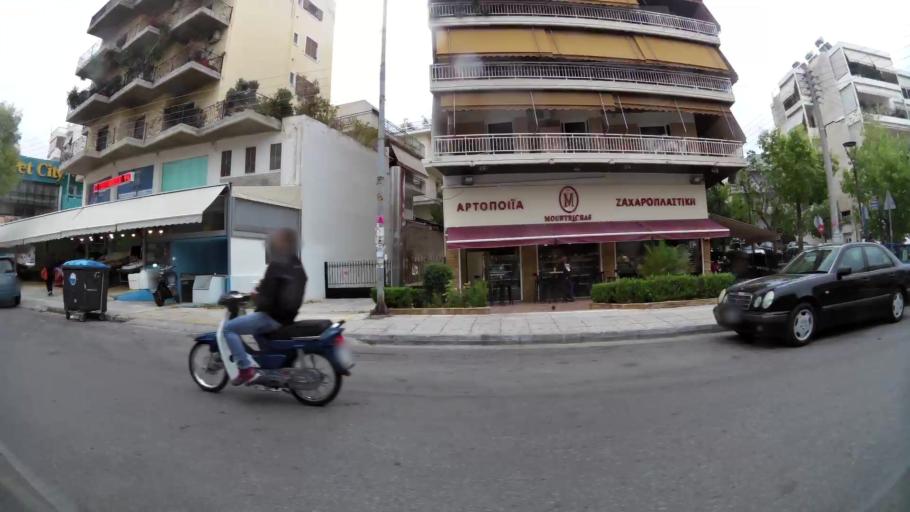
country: GR
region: Attica
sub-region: Nomarchia Athinas
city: Palaio Faliro
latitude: 37.9287
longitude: 23.7097
